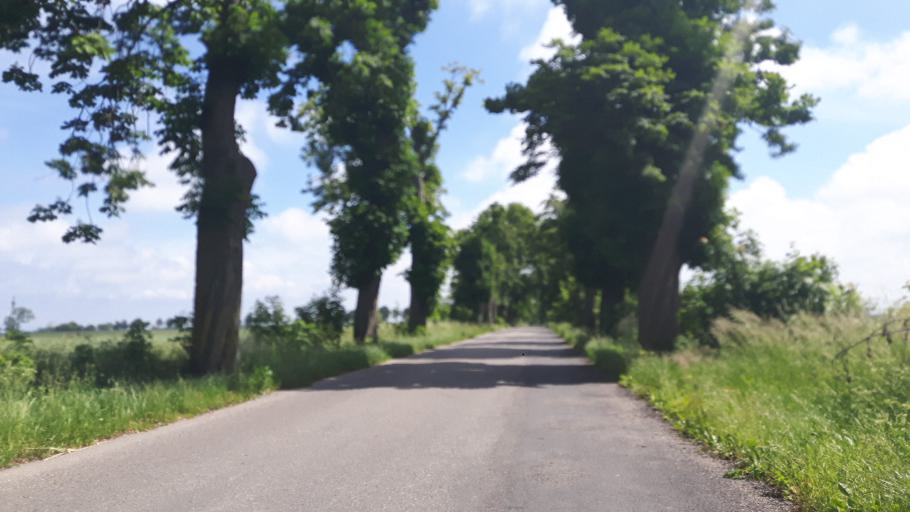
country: PL
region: West Pomeranian Voivodeship
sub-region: Powiat slawienski
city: Slawno
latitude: 54.5086
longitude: 16.5906
